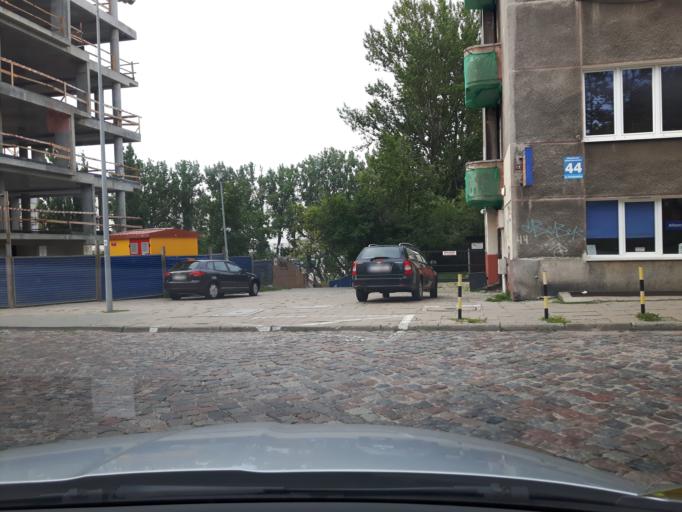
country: PL
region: Pomeranian Voivodeship
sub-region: Gdynia
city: Gdynia
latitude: 54.5077
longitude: 18.5390
